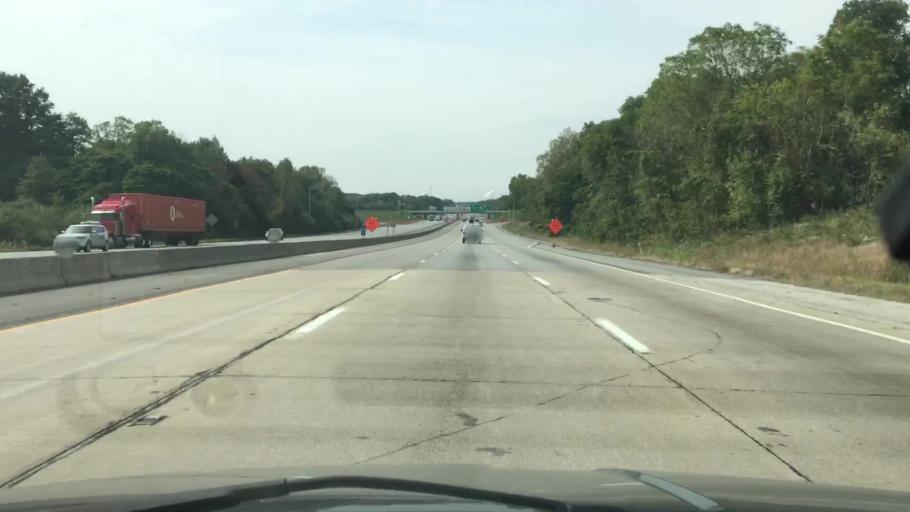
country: US
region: Indiana
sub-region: Porter County
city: Chesterton
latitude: 41.6250
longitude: -87.0371
